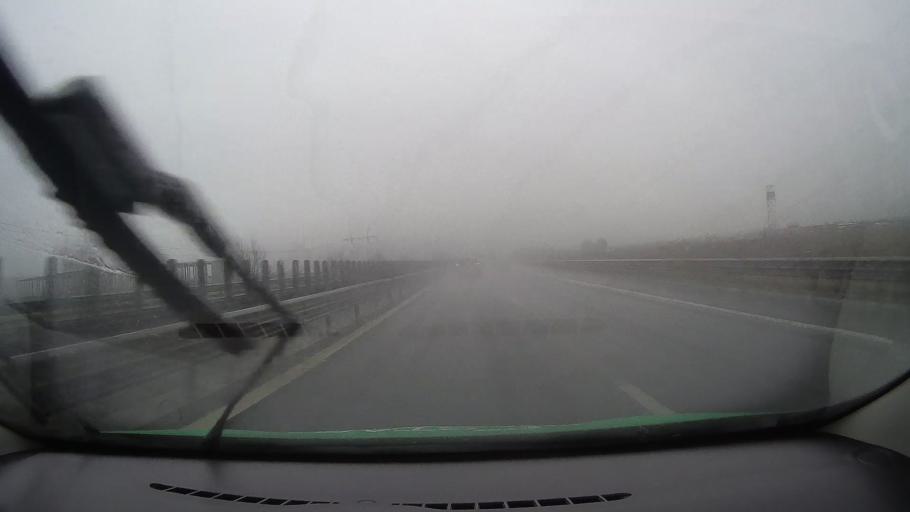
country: RO
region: Sibiu
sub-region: Municipiul Sibiu
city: Sibiu
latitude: 45.8244
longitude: 24.1445
